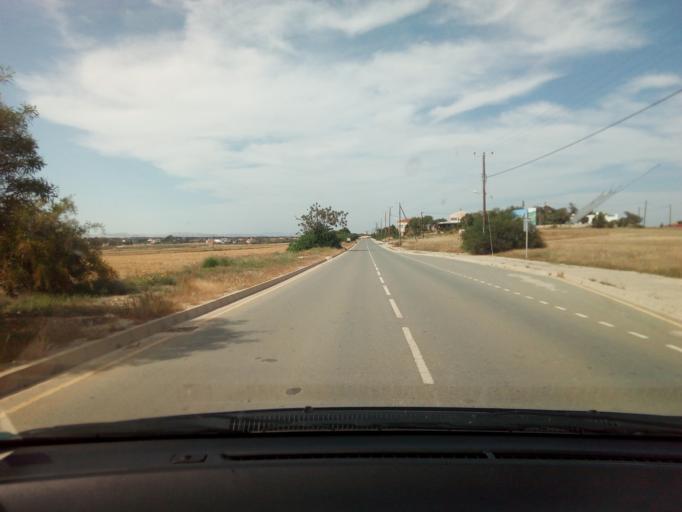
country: CY
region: Larnaka
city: Perivolia
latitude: 34.8219
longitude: 33.6009
